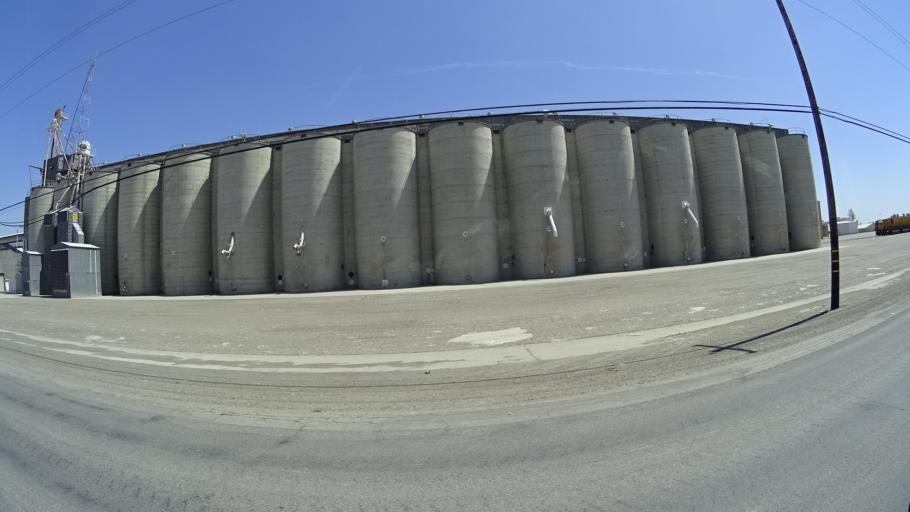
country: US
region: California
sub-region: Kings County
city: Corcoran
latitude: 36.0923
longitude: -119.5523
